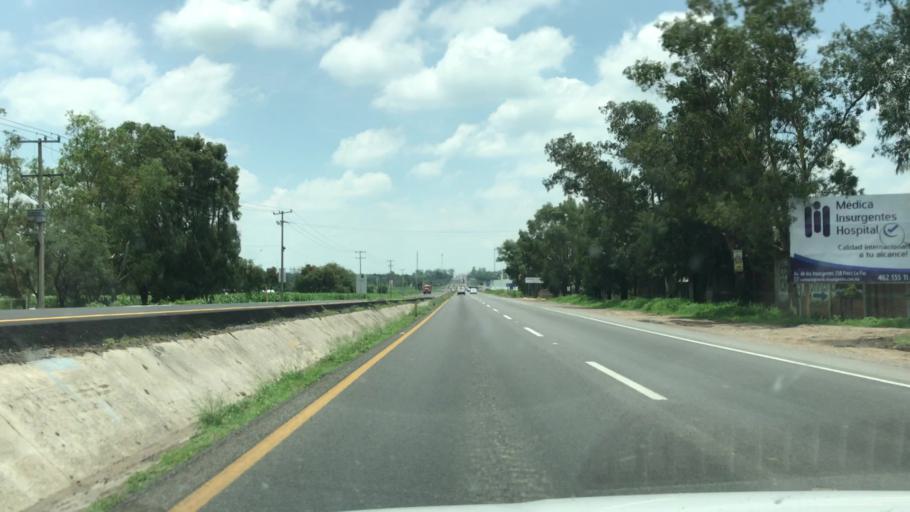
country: MX
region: Guanajuato
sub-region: Irapuato
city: San Ignacio de Rivera (Ojo de Agua)
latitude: 20.5464
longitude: -101.4543
